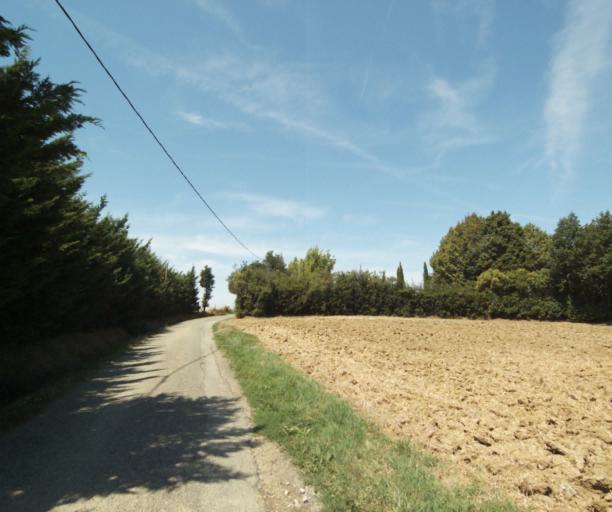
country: FR
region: Midi-Pyrenees
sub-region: Departement de l'Ariege
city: Lezat-sur-Leze
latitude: 43.2675
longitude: 1.3115
